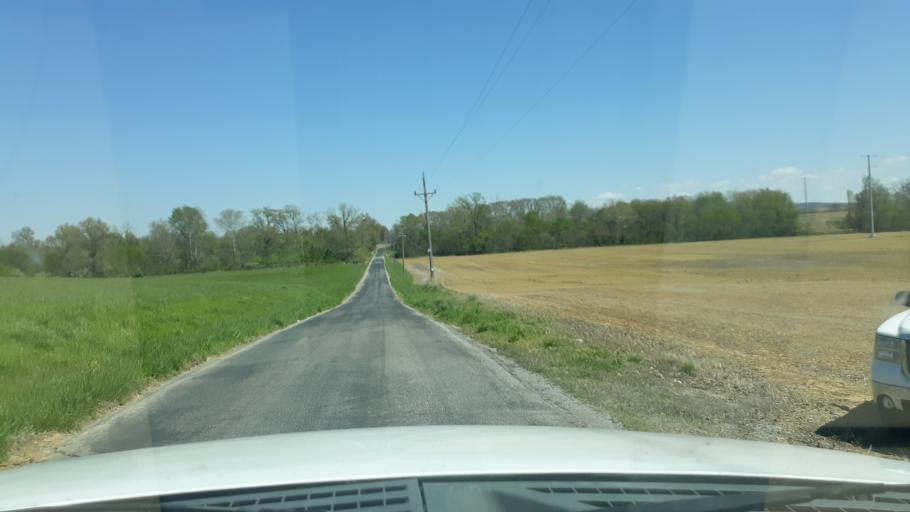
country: US
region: Illinois
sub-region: Saline County
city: Harrisburg
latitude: 37.8341
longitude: -88.6231
